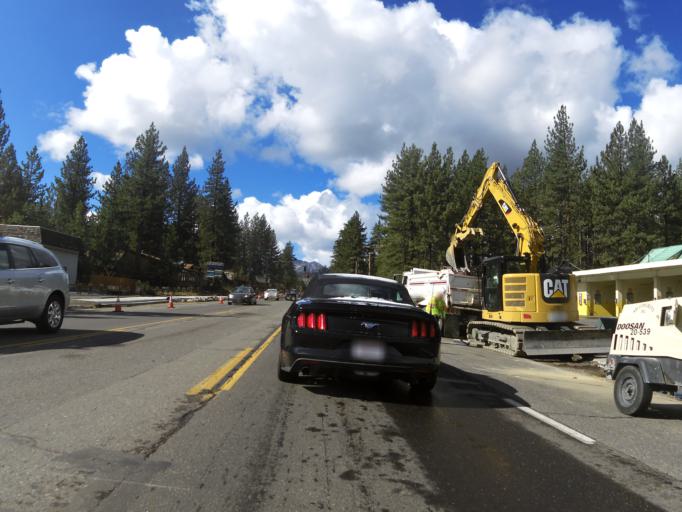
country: US
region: California
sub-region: El Dorado County
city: South Lake Tahoe
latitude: 38.9197
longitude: -119.9948
